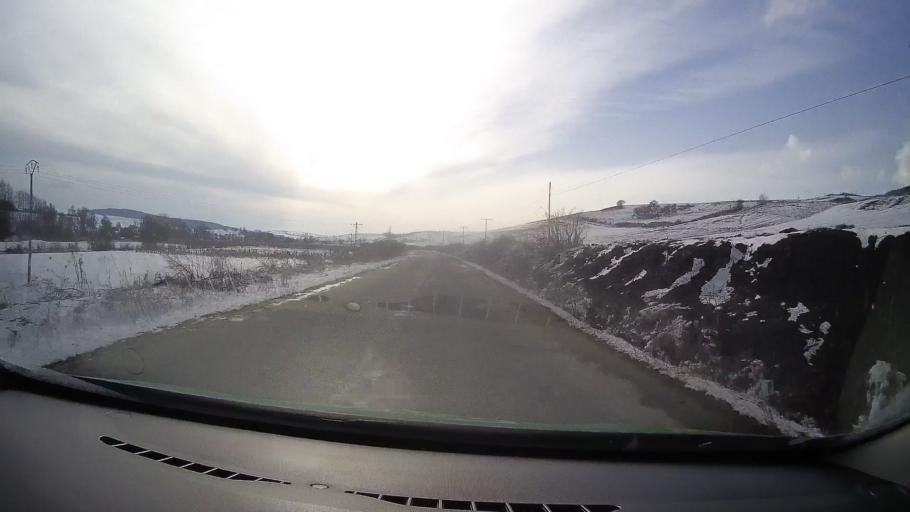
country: RO
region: Sibiu
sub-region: Oras Agnita
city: Ruja
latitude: 46.0149
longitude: 24.6909
